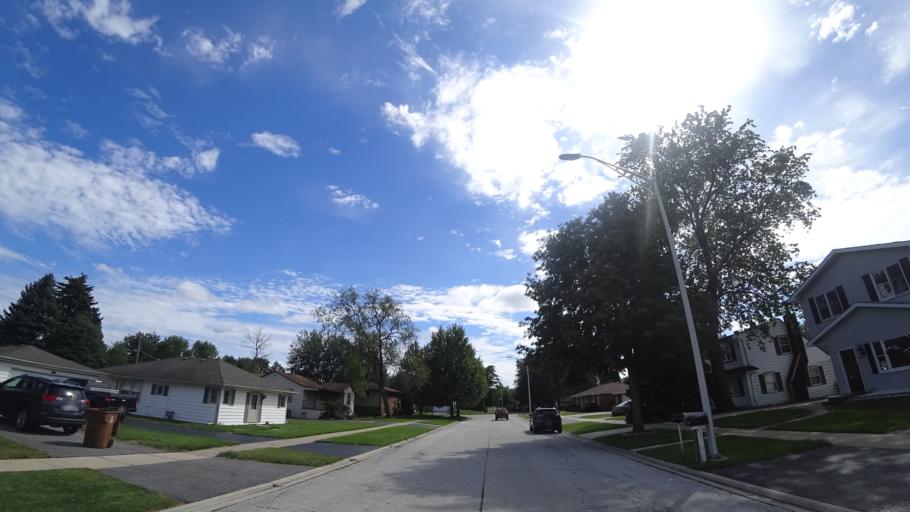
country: US
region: Illinois
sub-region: Cook County
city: Chicago Ridge
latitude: 41.7132
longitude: -87.7723
